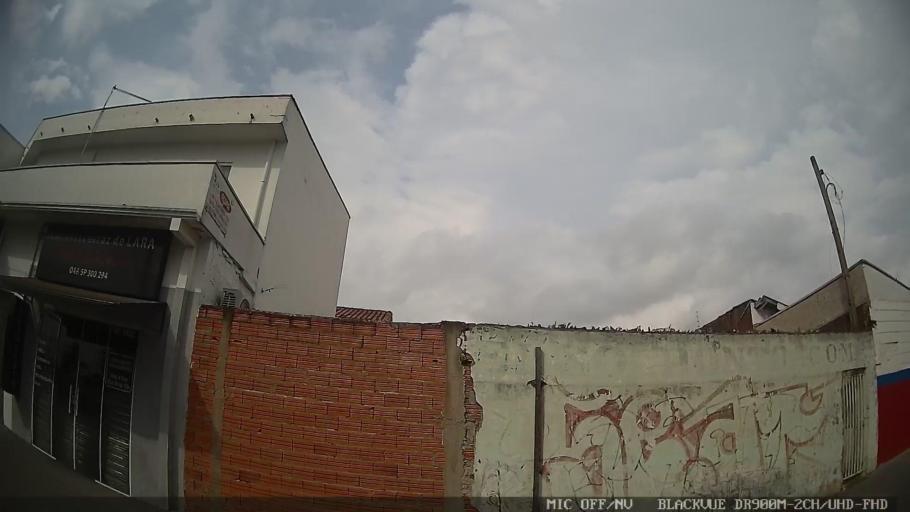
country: BR
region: Sao Paulo
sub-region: Indaiatuba
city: Indaiatuba
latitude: -23.1140
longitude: -47.2402
